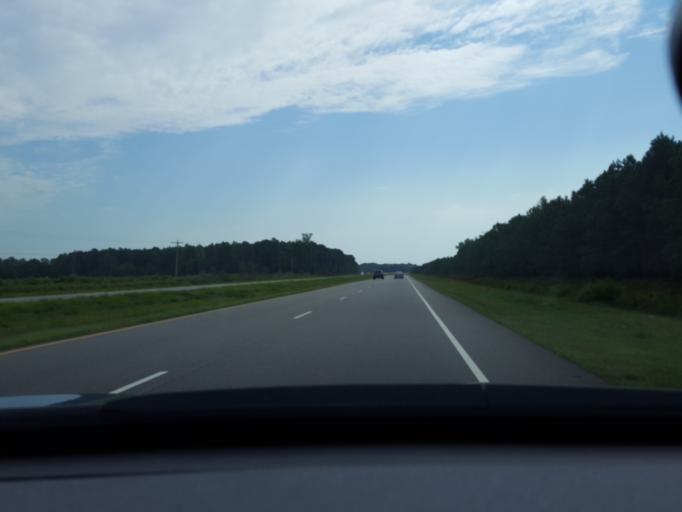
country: US
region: North Carolina
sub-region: Chowan County
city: Edenton
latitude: 36.0375
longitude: -76.7348
